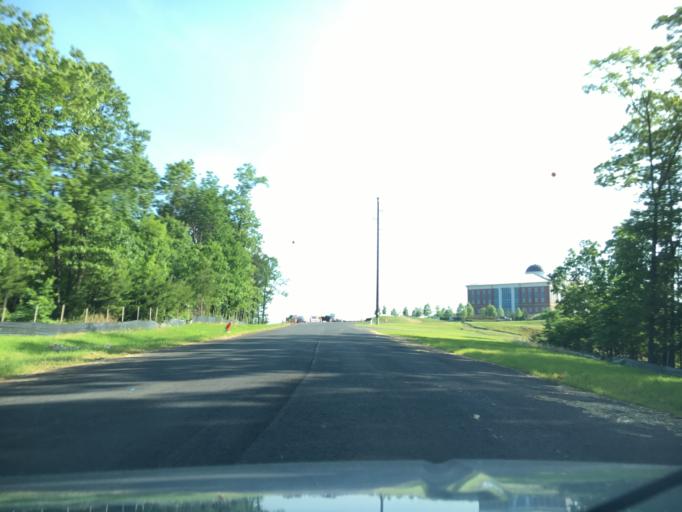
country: US
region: Virginia
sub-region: City of Lynchburg
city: West Lynchburg
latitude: 37.3349
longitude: -79.1820
